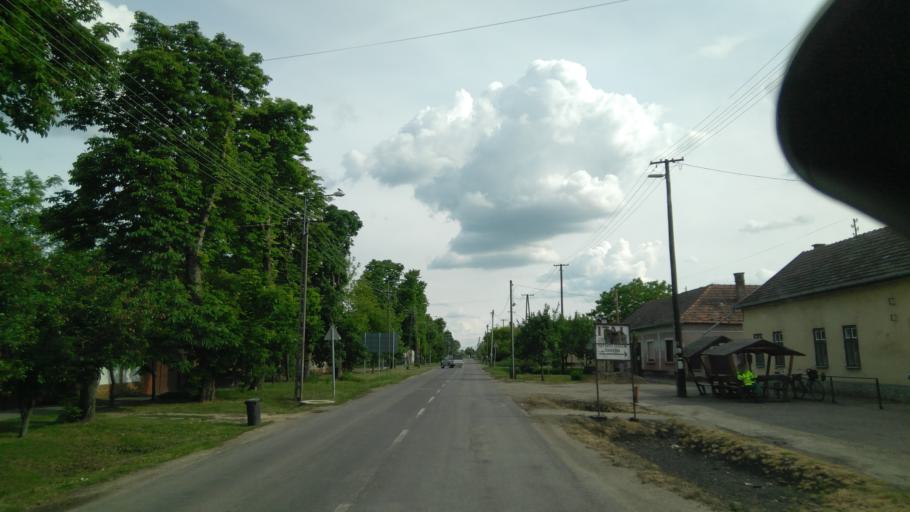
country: HU
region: Bekes
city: Battonya
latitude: 46.2914
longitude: 21.0170
